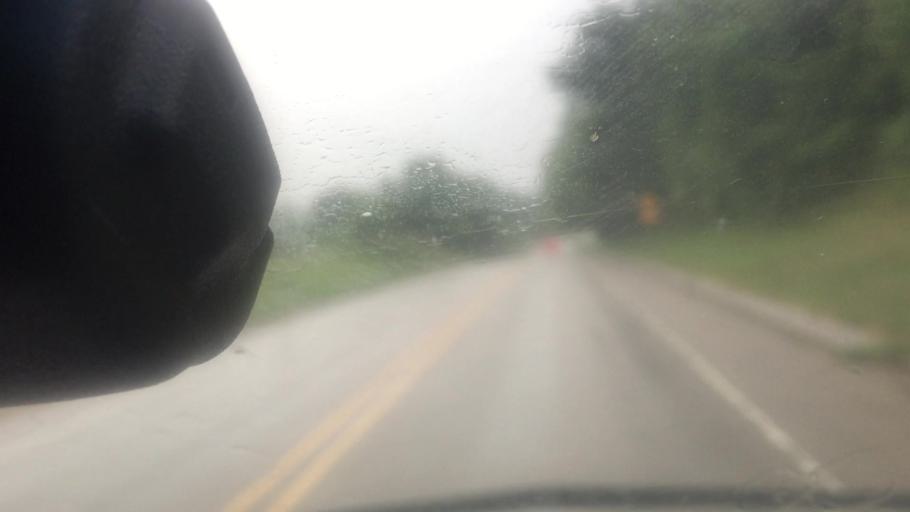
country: US
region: Illinois
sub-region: Madison County
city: Edwardsville
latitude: 38.8290
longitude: -89.9308
